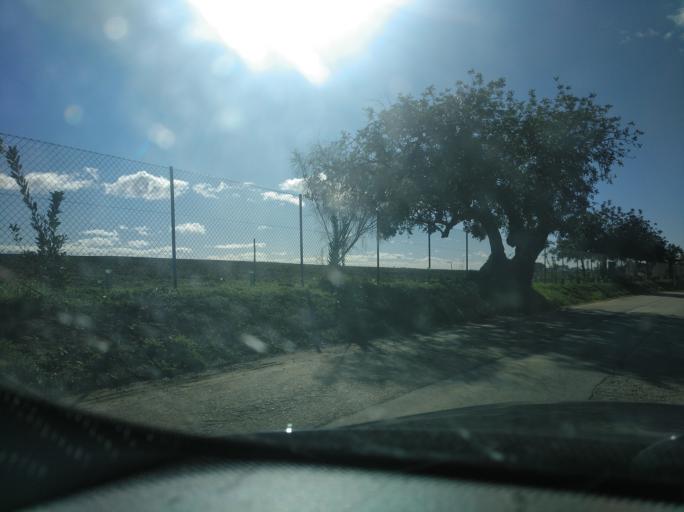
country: PT
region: Faro
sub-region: Vila Real de Santo Antonio
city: Monte Gordo
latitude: 37.1657
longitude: -7.5414
